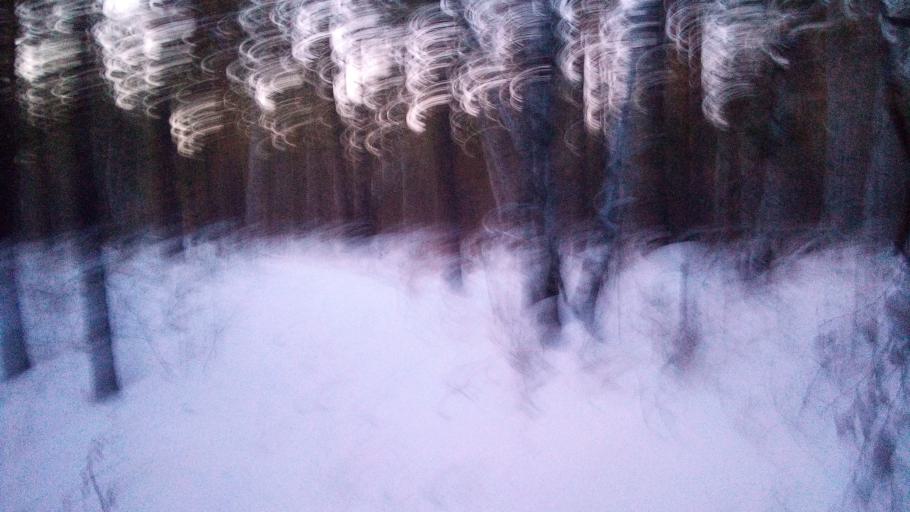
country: RU
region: Chelyabinsk
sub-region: Gorod Chelyabinsk
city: Chelyabinsk
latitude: 55.1634
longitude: 61.3324
